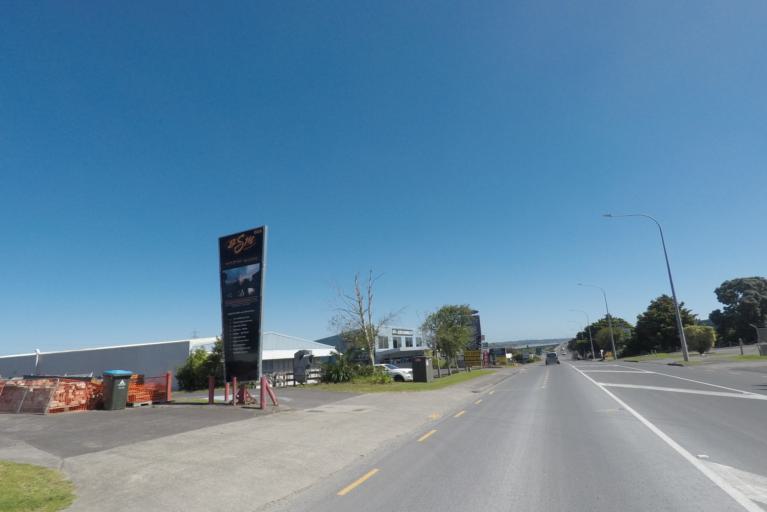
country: NZ
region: Auckland
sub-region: Auckland
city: Rosebank
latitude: -36.8696
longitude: 174.6663
